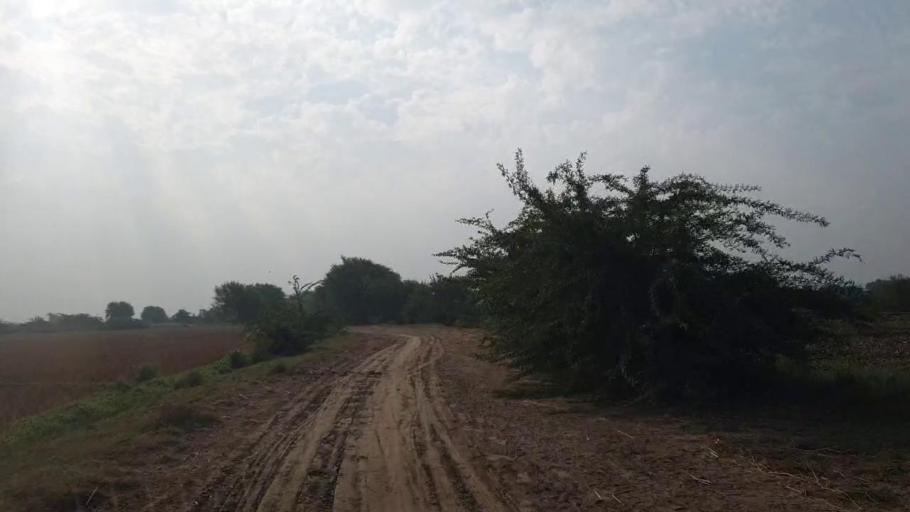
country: PK
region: Sindh
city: Tando Bago
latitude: 24.7864
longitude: 68.8791
